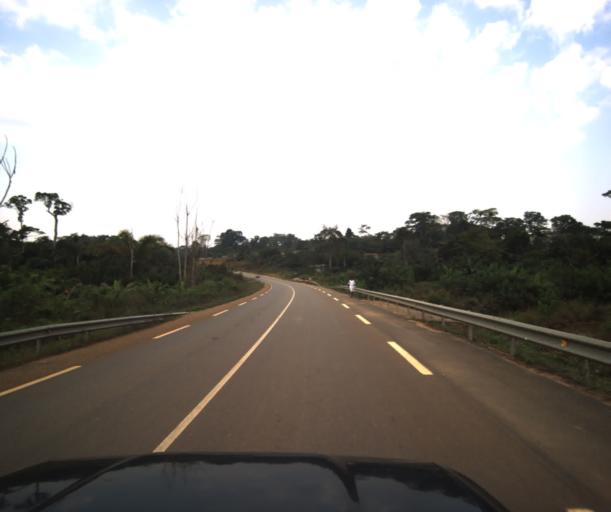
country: CM
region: Centre
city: Akono
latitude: 3.6186
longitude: 11.3189
